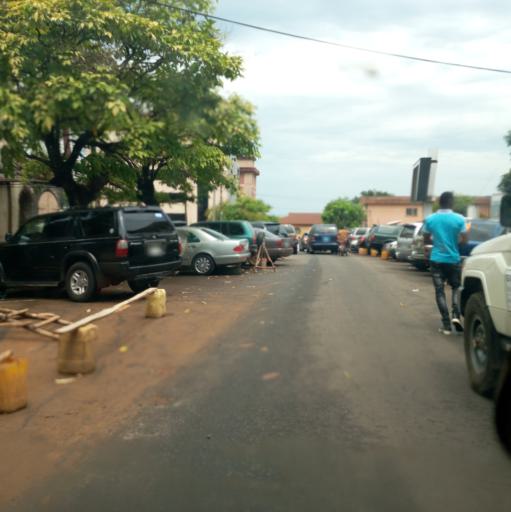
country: SL
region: Western Area
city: Freetown
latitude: 8.4885
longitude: -13.2359
